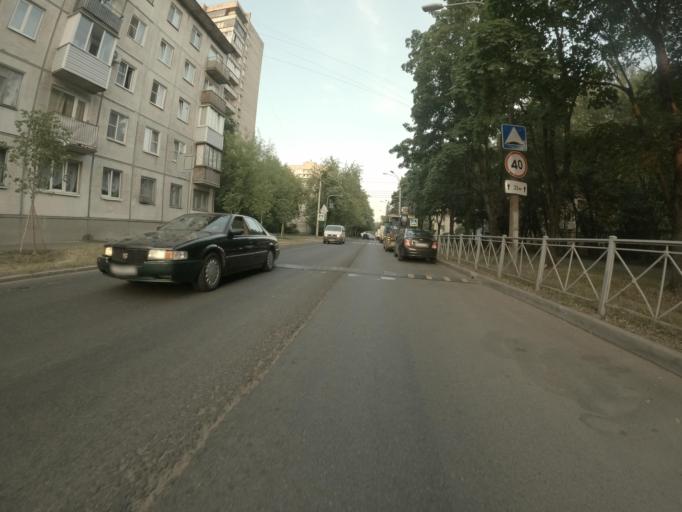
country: RU
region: Leningrad
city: Kalininskiy
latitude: 59.9872
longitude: 30.4214
